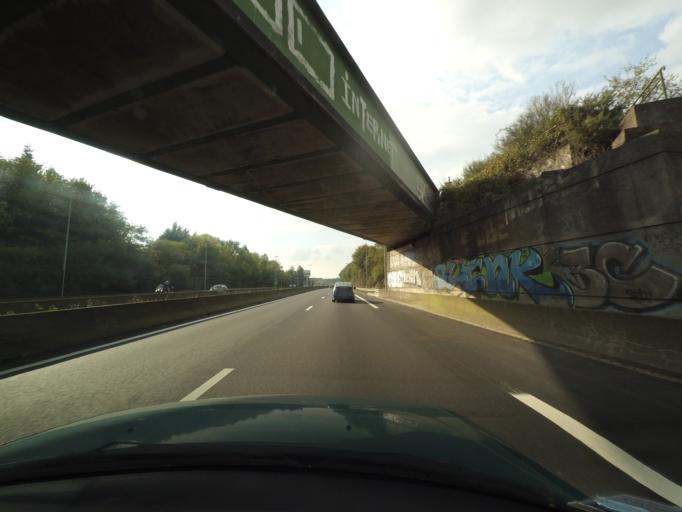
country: FR
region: Pays de la Loire
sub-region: Departement de la Loire-Atlantique
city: La Chapelle-sur-Erdre
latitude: 47.2568
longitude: -1.5424
